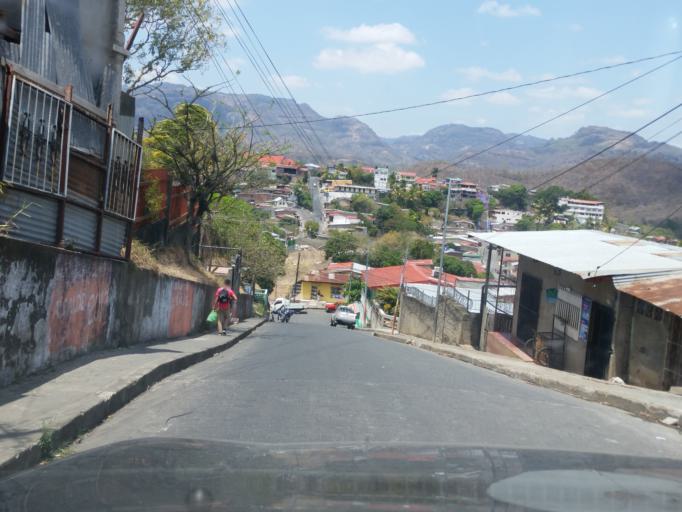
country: NI
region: Boaco
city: Boaco
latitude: 12.4698
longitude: -85.6564
